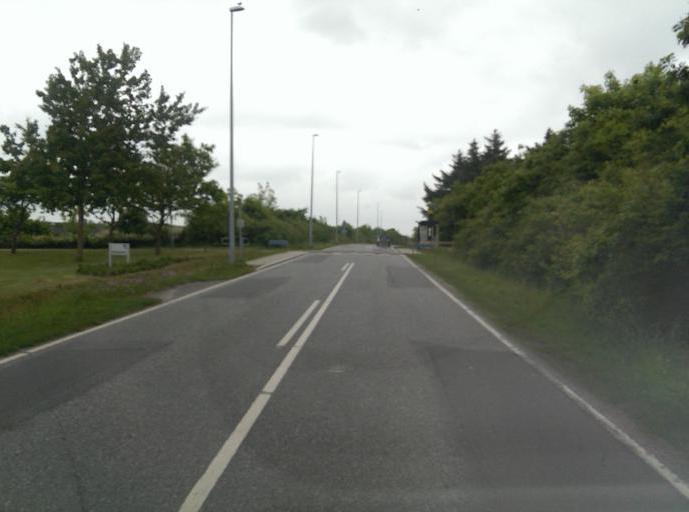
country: DK
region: South Denmark
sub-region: Fano Kommune
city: Nordby
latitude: 55.5281
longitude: 8.3687
